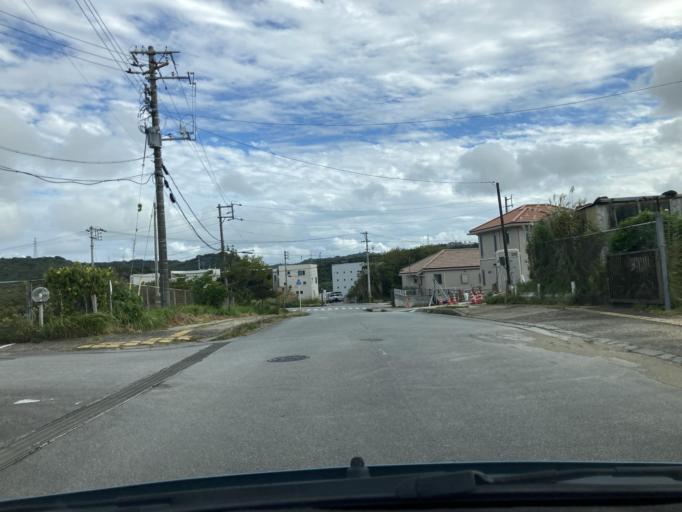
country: JP
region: Okinawa
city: Tomigusuku
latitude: 26.1755
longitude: 127.7443
